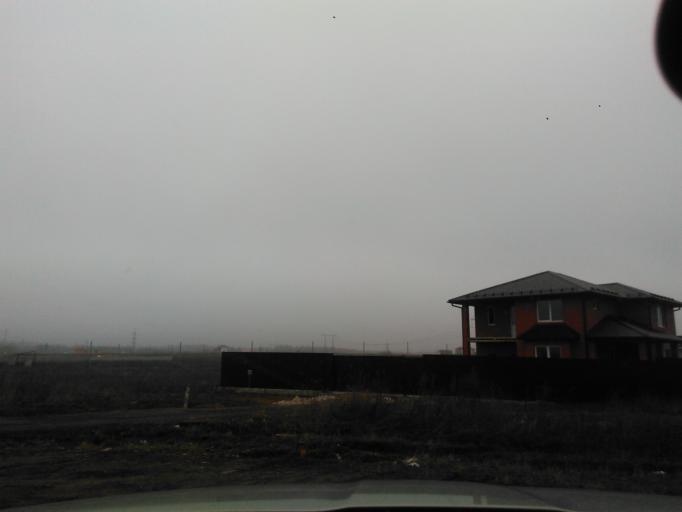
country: RU
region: Moskovskaya
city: Dedovsk
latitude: 55.9183
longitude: 37.1575
